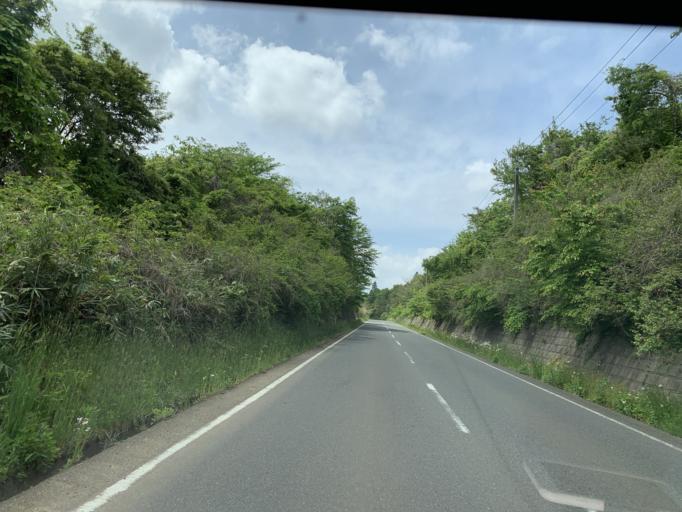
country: JP
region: Iwate
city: Ichinoseki
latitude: 38.8079
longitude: 141.0120
